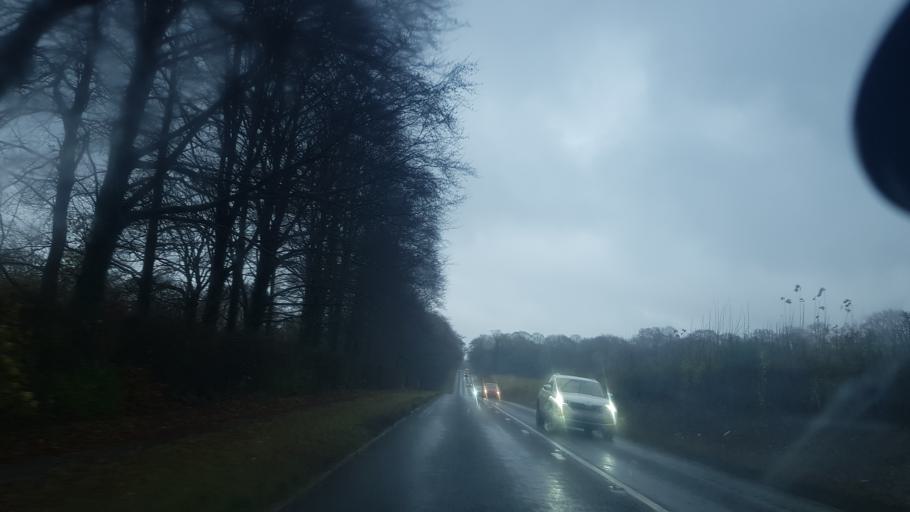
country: GB
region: England
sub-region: Surrey
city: East Horsley
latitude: 51.2555
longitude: -0.4676
